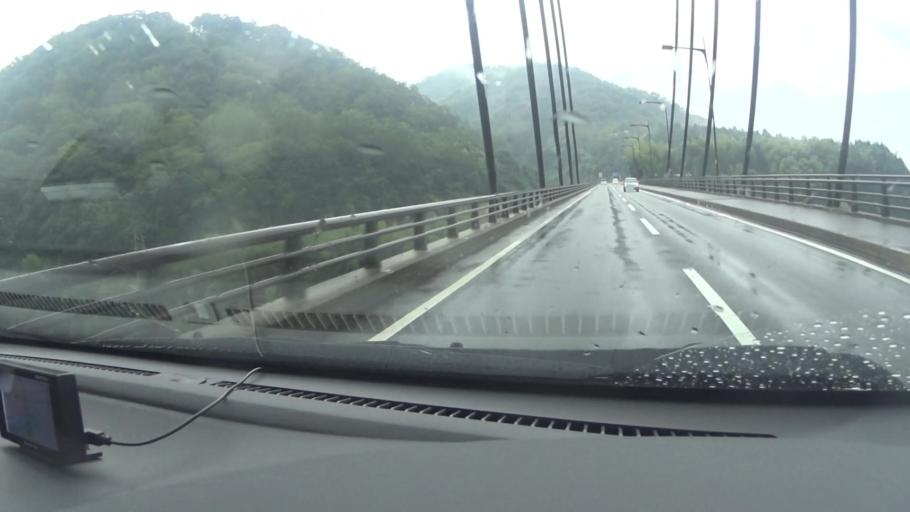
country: JP
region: Kyoto
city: Ayabe
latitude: 35.2911
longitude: 135.2670
